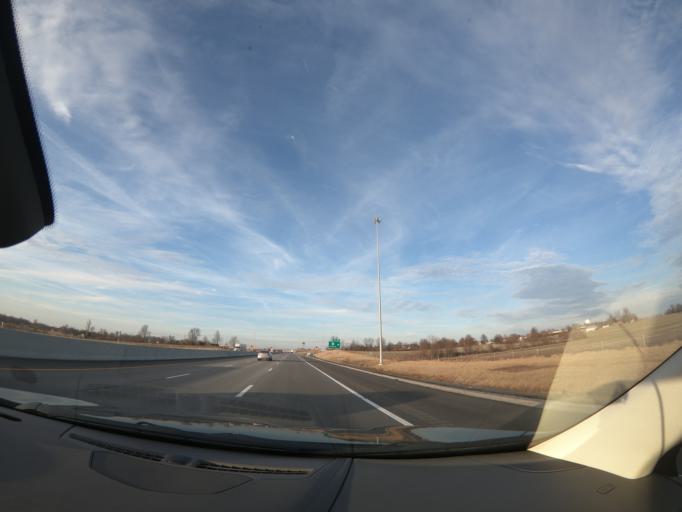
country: US
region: Kentucky
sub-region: Larue County
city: Hodgenville
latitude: 37.5156
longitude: -85.8860
